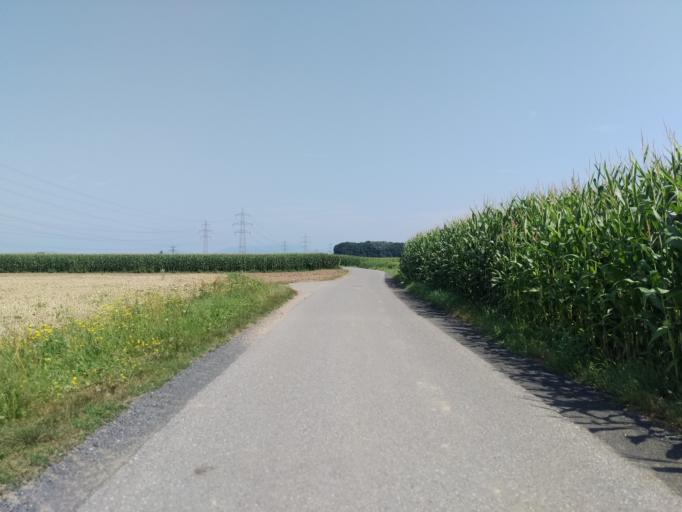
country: AT
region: Styria
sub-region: Politischer Bezirk Graz-Umgebung
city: Werndorf
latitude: 46.9298
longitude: 15.4899
